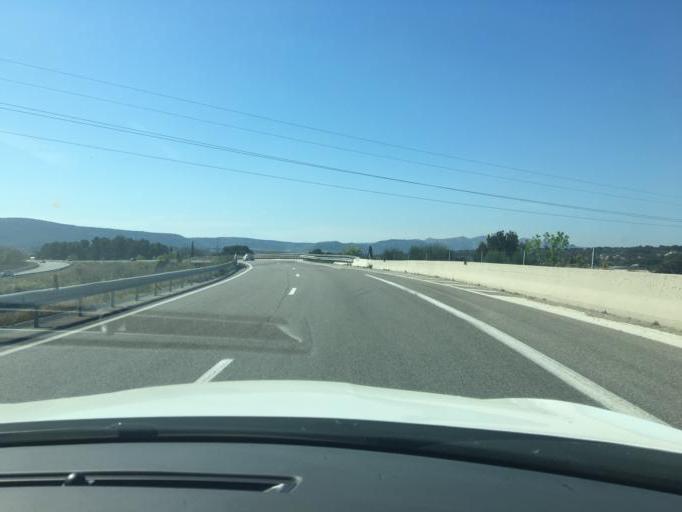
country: FR
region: Provence-Alpes-Cote d'Azur
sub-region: Departement des Bouches-du-Rhone
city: Roquevaire
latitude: 43.3196
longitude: 5.5916
